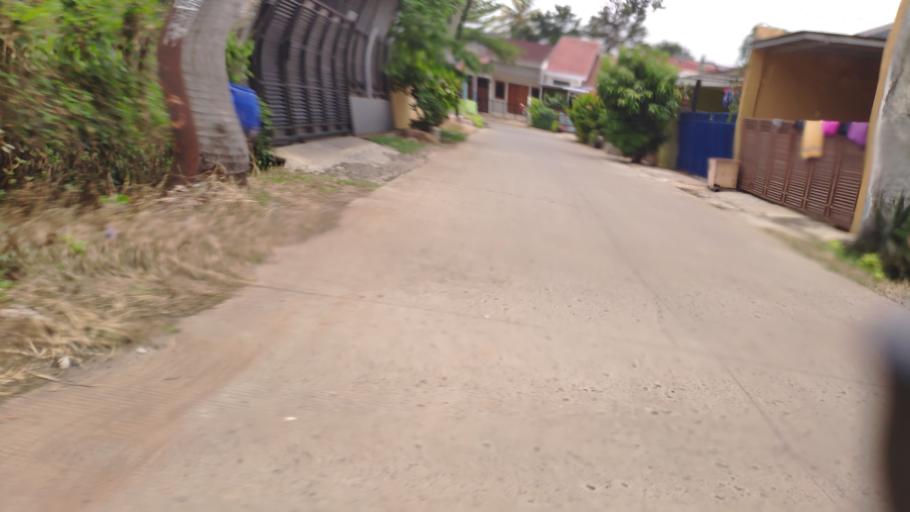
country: ID
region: West Java
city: Sawangan
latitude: -6.3840
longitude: 106.7856
